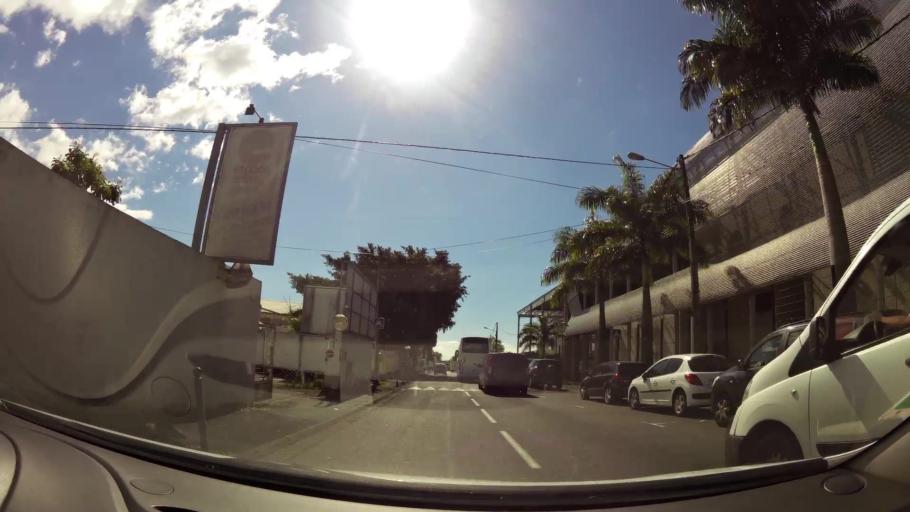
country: RE
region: Reunion
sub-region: Reunion
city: Saint-Denis
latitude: -20.8937
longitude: 55.4972
